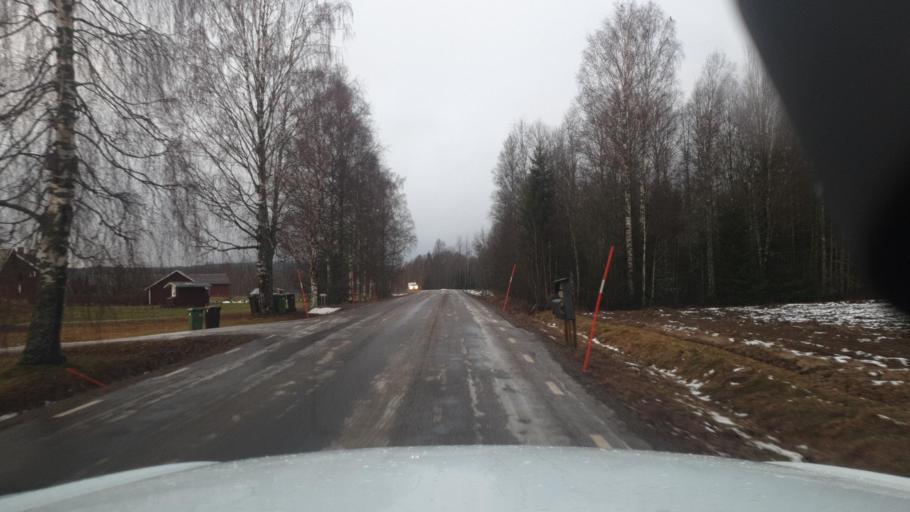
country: SE
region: Vaermland
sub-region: Torsby Kommun
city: Torsby
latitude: 59.9851
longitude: 12.8677
